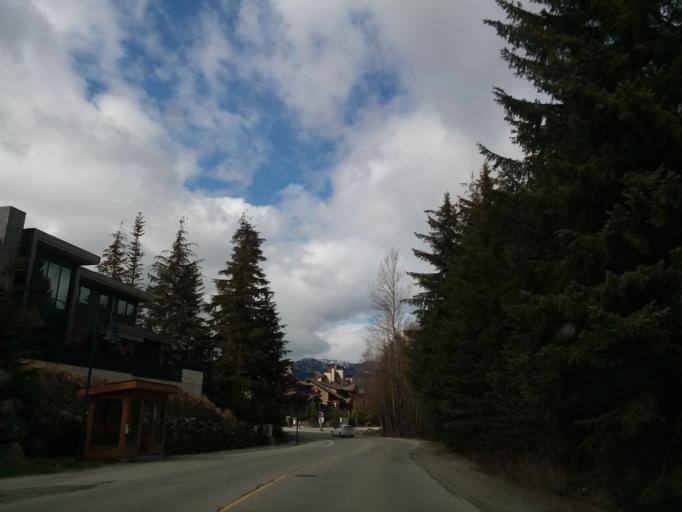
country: CA
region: British Columbia
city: Whistler
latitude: 50.1253
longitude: -122.9546
